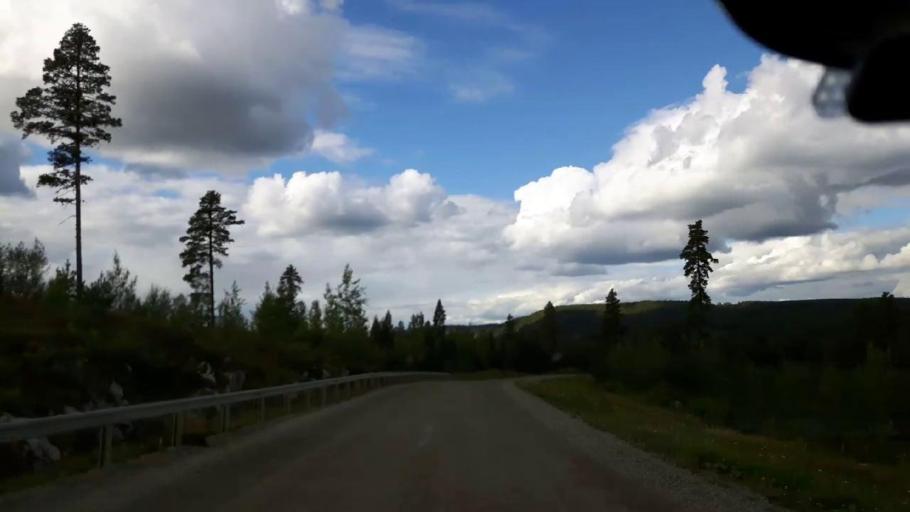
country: SE
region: Jaemtland
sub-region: Stroemsunds Kommun
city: Stroemsund
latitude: 63.4058
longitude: 15.5642
